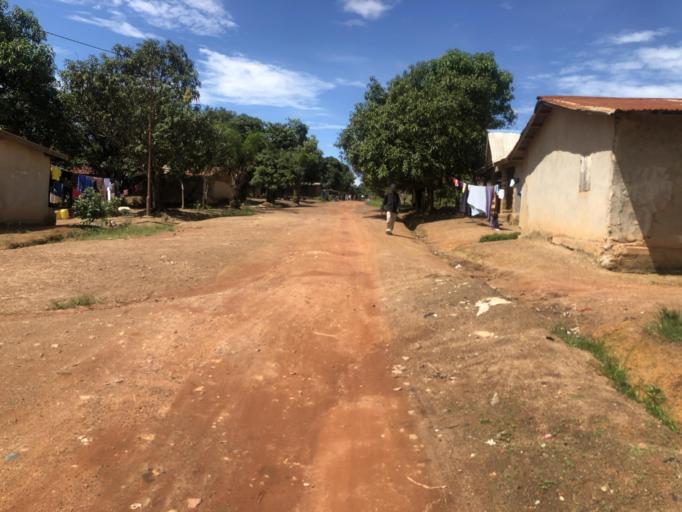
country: SL
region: Eastern Province
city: Koidu
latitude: 8.6390
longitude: -10.9528
